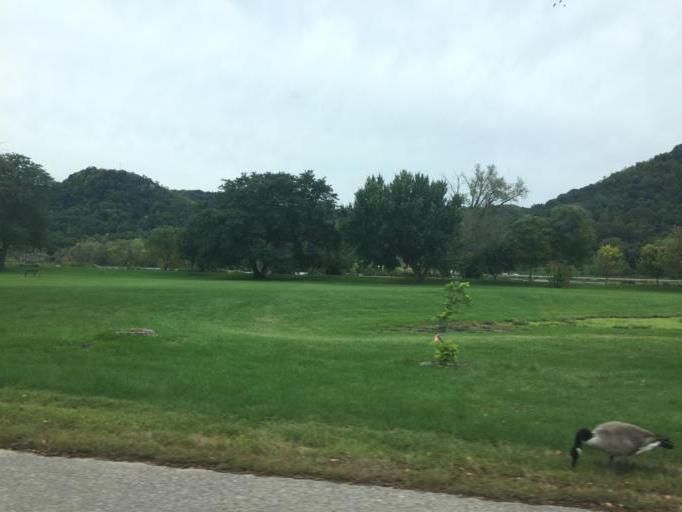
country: US
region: Minnesota
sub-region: Winona County
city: Winona
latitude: 44.0443
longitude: -91.6549
